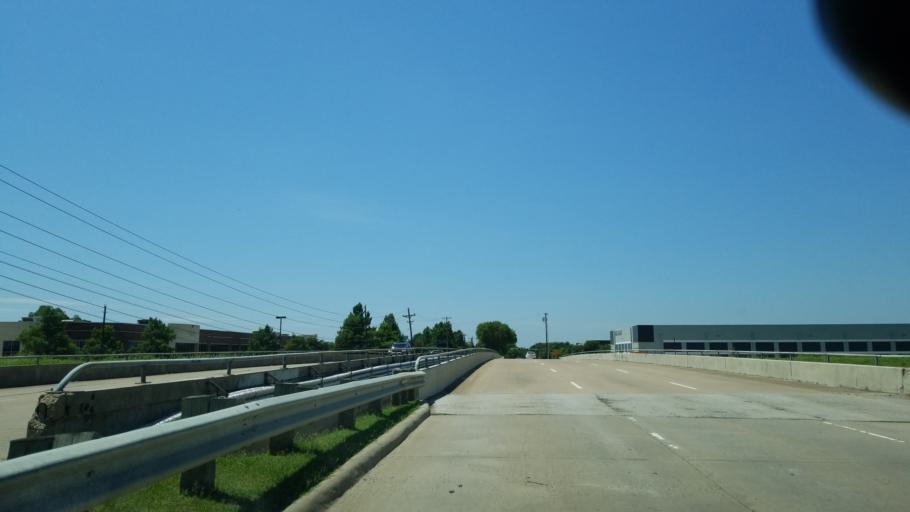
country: US
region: Texas
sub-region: Dallas County
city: Carrollton
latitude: 32.9478
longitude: -96.9251
